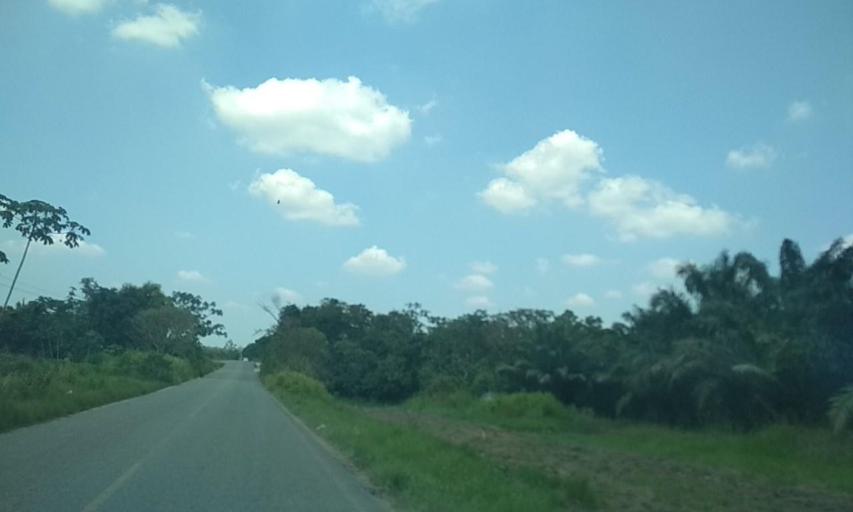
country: MX
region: Tabasco
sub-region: Huimanguillo
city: Paso de la Mina 2da. Seccion (Barrial)
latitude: 17.7601
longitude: -93.6568
